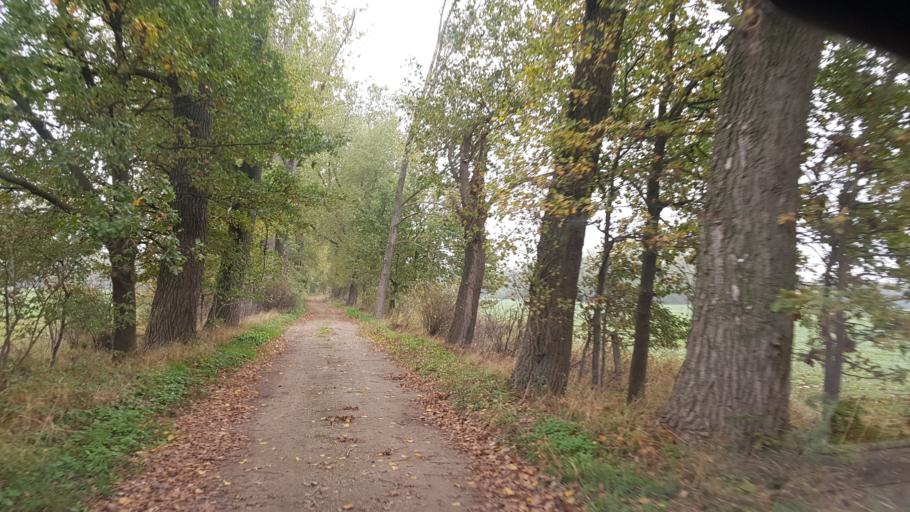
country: DE
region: Brandenburg
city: Schonewalde
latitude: 51.6888
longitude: 13.6007
